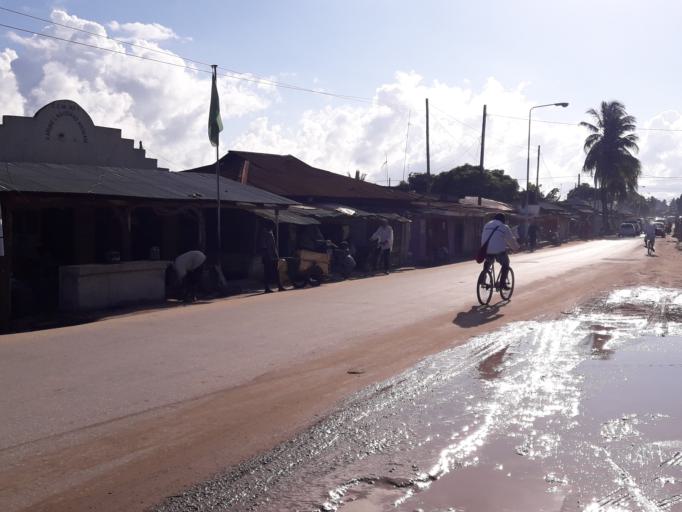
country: TZ
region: Zanzibar Urban/West
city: Zanzibar
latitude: -6.1759
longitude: 39.2099
